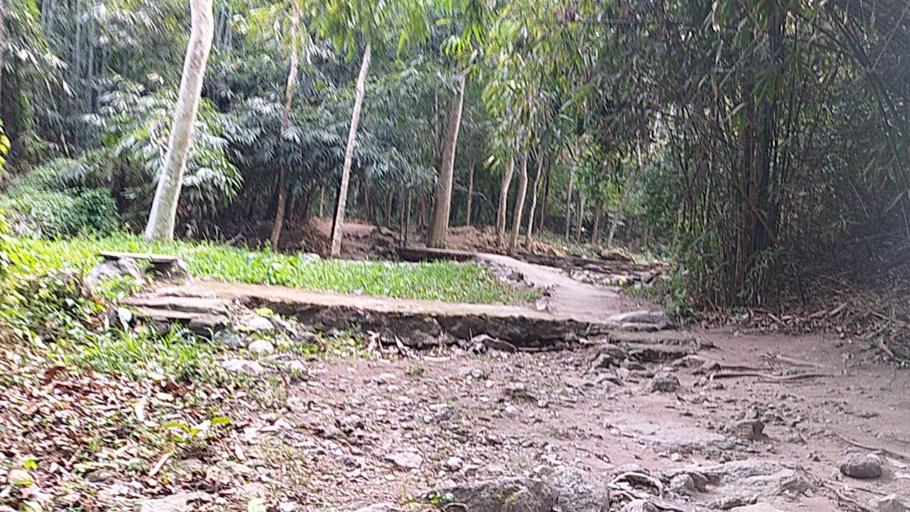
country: TH
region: Sara Buri
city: Wihan Daeng
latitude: 14.4354
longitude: 100.9627
